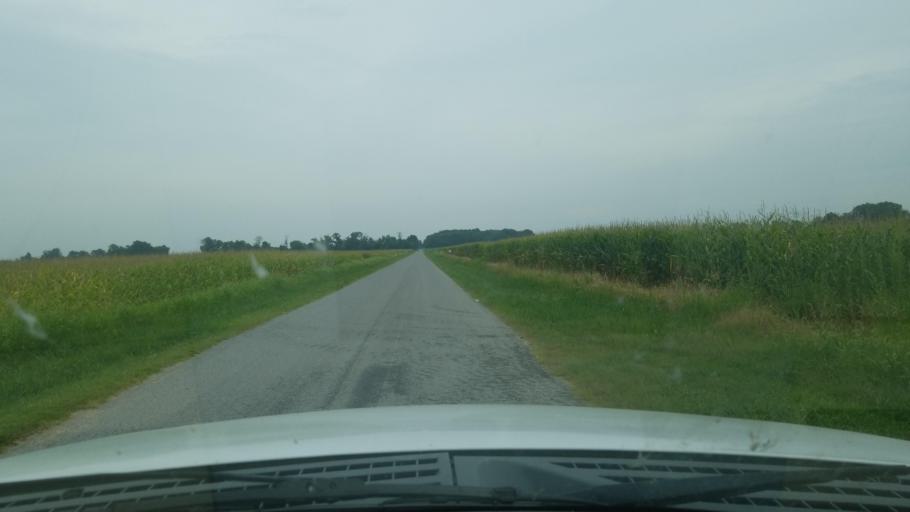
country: US
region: Illinois
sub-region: Saline County
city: Eldorado
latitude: 37.8630
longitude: -88.5027
